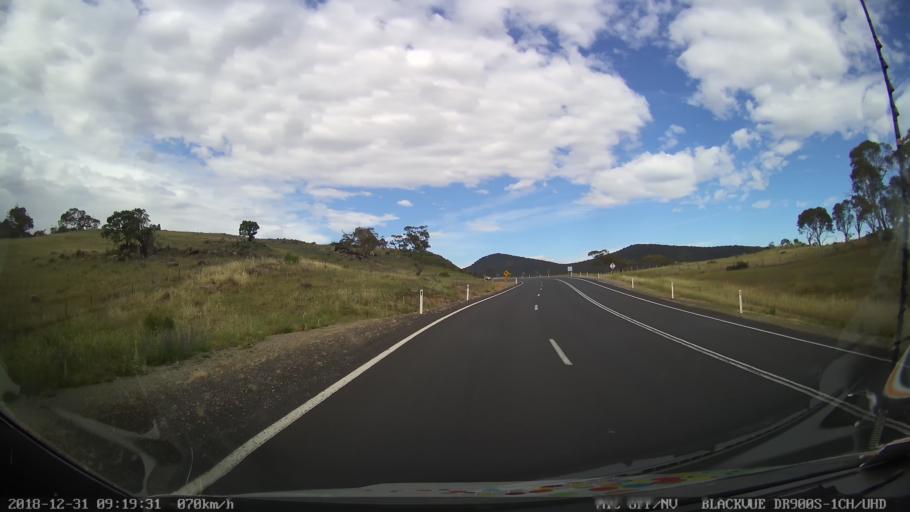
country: AU
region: New South Wales
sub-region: Snowy River
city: Jindabyne
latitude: -36.4159
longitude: 148.5850
